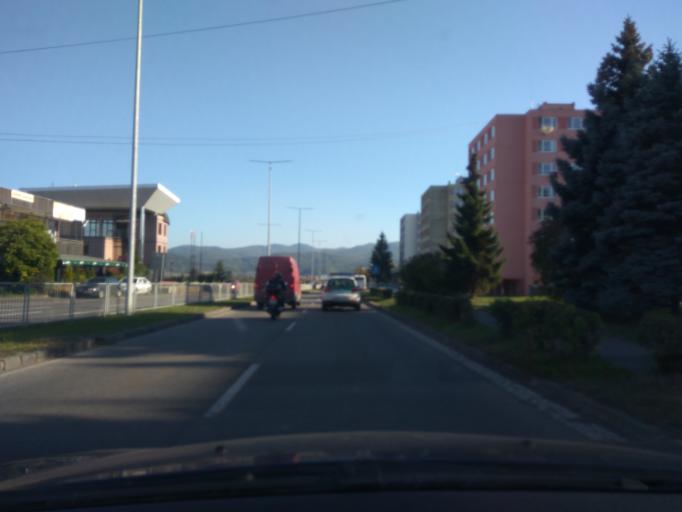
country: SK
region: Banskobystricky
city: Ziar nad Hronom
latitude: 48.5927
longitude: 18.8522
